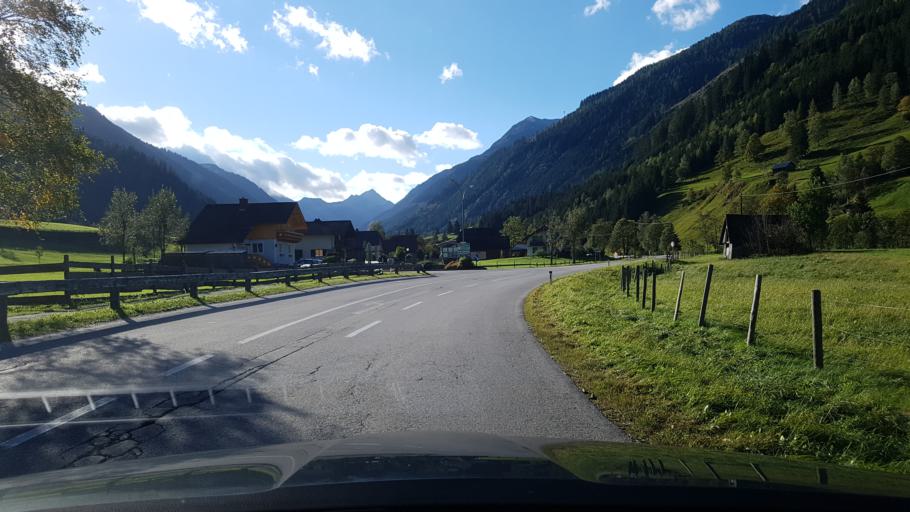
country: AT
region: Styria
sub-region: Politischer Bezirk Liezen
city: Sankt Nikolai im Solktal
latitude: 47.3481
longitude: 14.0278
